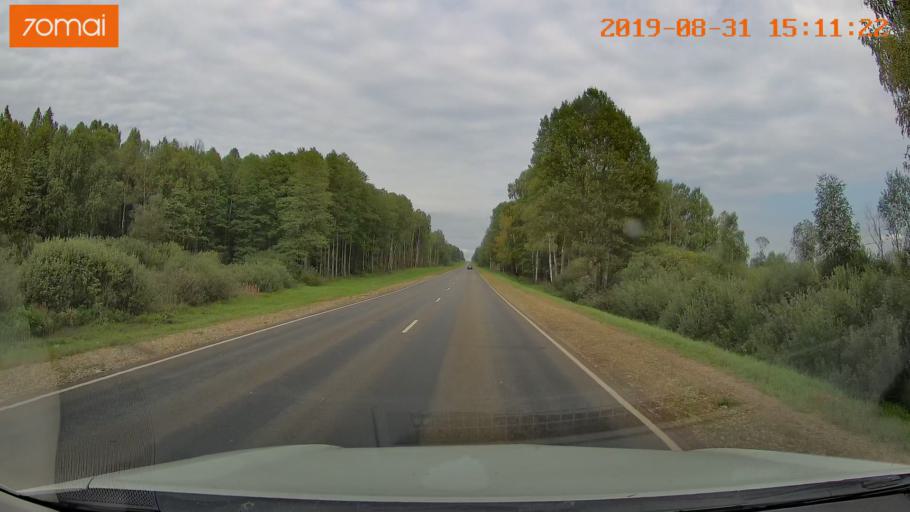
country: RU
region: Kaluga
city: Spas-Demensk
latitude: 54.4219
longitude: 34.2419
